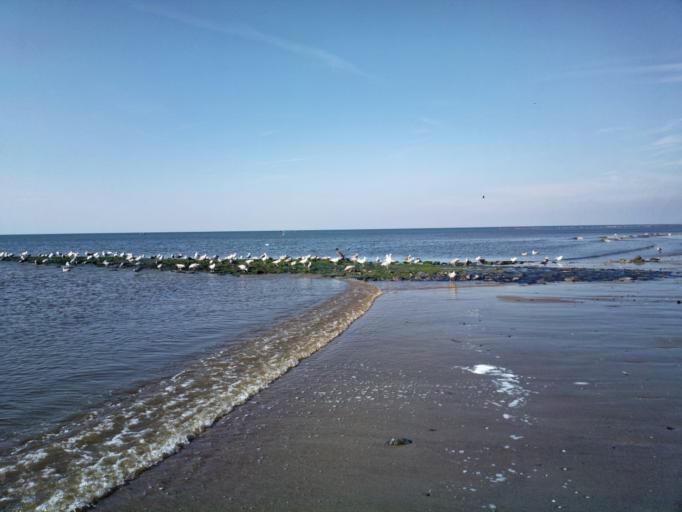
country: NL
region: North Holland
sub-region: Gemeente Texel
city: Den Burg
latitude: 53.0672
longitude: 4.7239
